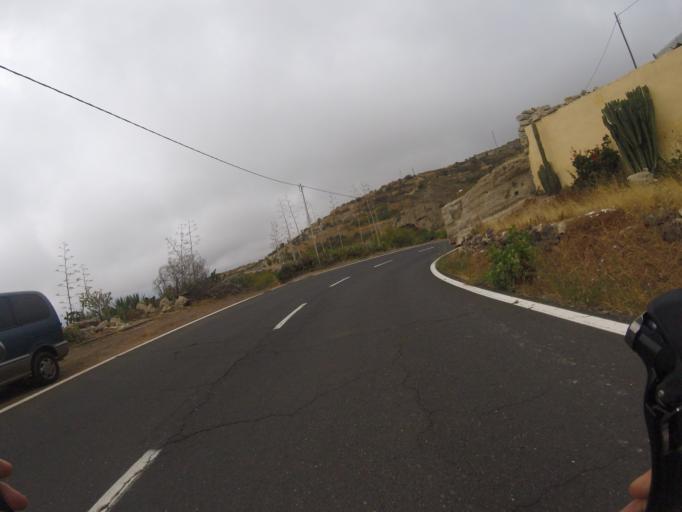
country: ES
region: Canary Islands
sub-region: Provincia de Santa Cruz de Tenerife
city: Fasnia
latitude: 28.2241
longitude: -16.4491
